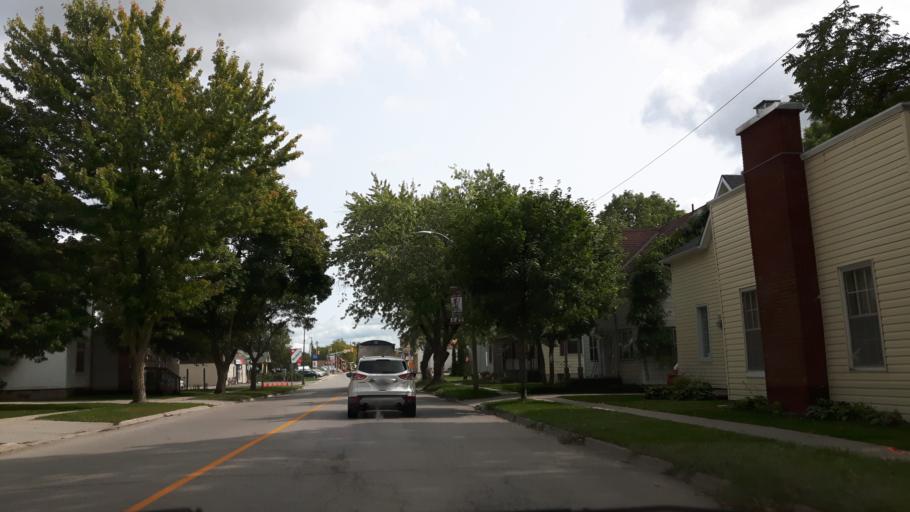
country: CA
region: Ontario
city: Huron East
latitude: 43.5543
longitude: -81.3956
